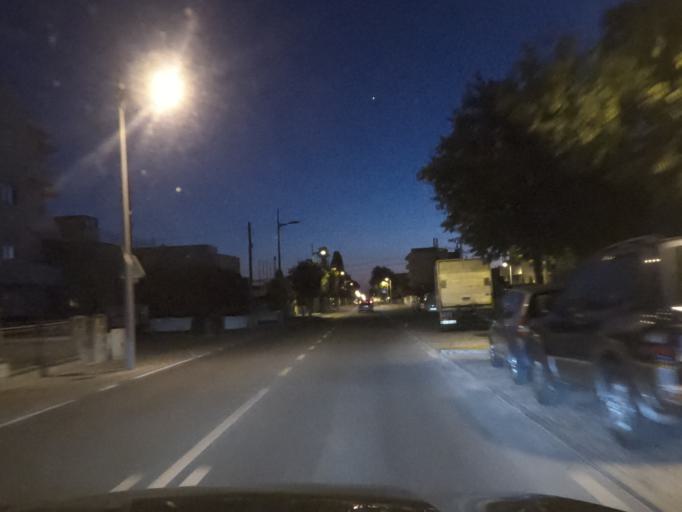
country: PT
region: Faro
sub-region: Loule
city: Loule
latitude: 37.1374
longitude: -8.0041
